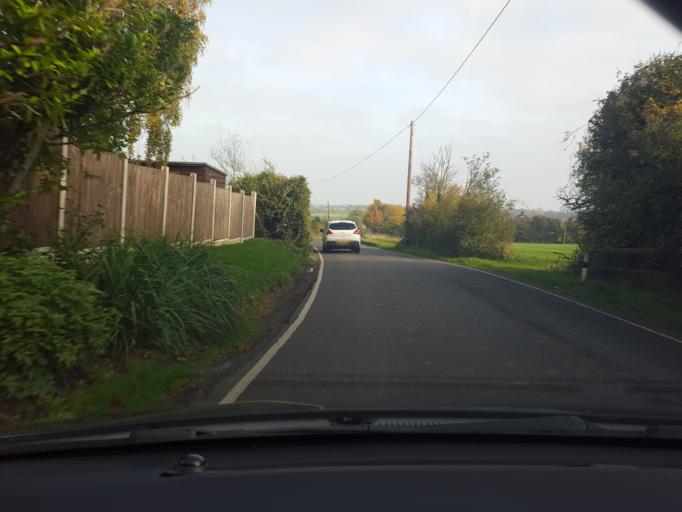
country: GB
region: England
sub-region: Essex
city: Frinton-on-Sea
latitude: 51.8573
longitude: 1.2042
